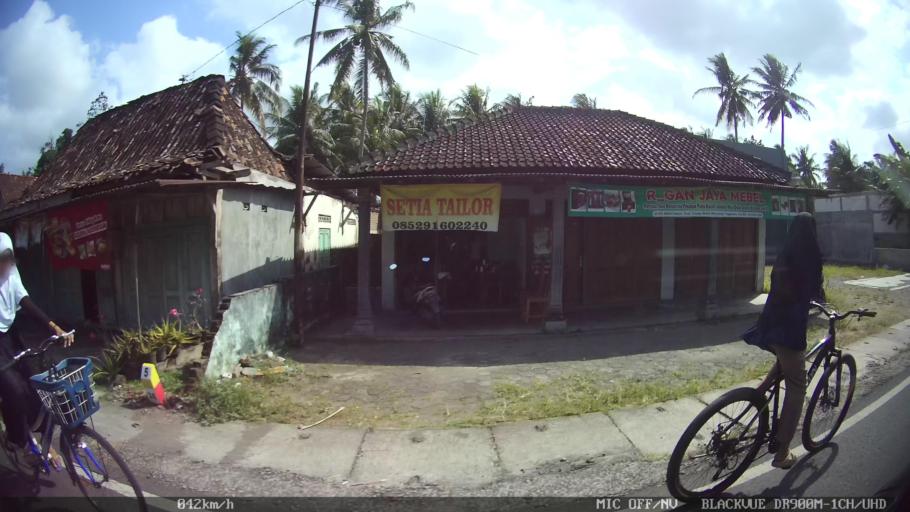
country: ID
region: Daerah Istimewa Yogyakarta
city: Srandakan
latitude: -7.8932
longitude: 110.1378
